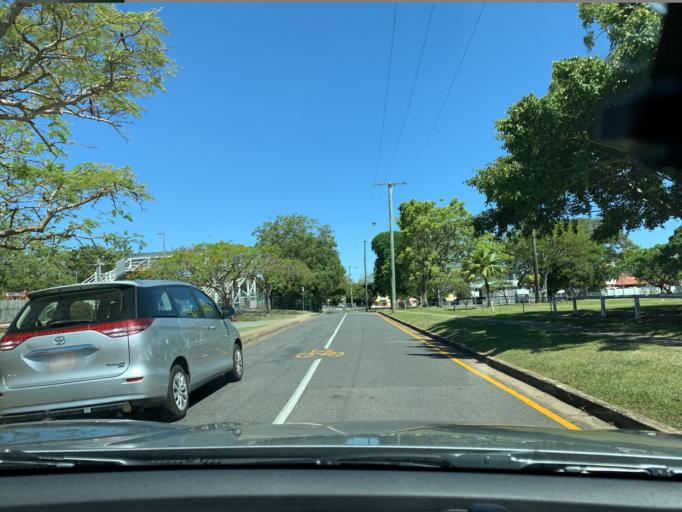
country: AU
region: Queensland
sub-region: Brisbane
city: Ascot
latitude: -27.4296
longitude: 153.0631
